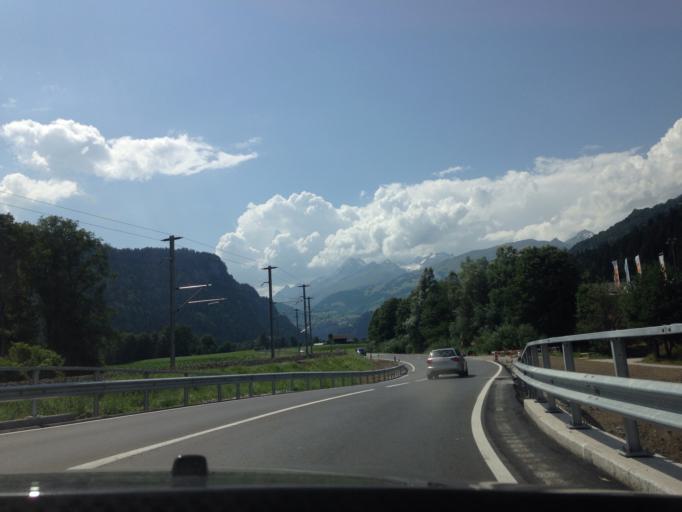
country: CH
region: Grisons
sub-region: Surselva District
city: Ilanz
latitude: 46.7739
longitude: 9.1933
